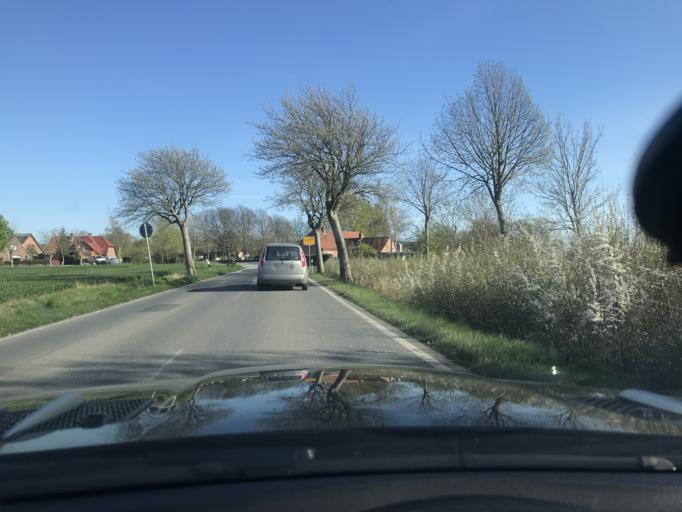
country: DE
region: Schleswig-Holstein
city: Grossenbrode
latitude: 54.4733
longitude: 11.0887
